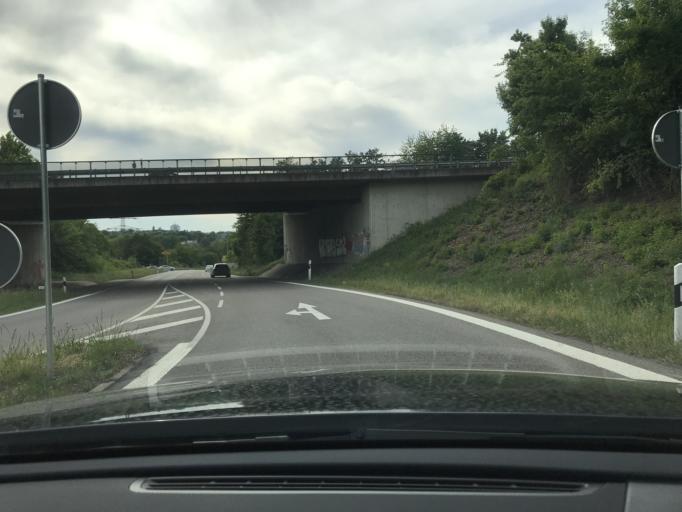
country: DE
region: Baden-Wuerttemberg
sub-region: Regierungsbezirk Stuttgart
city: Waiblingen
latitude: 48.8292
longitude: 9.3338
